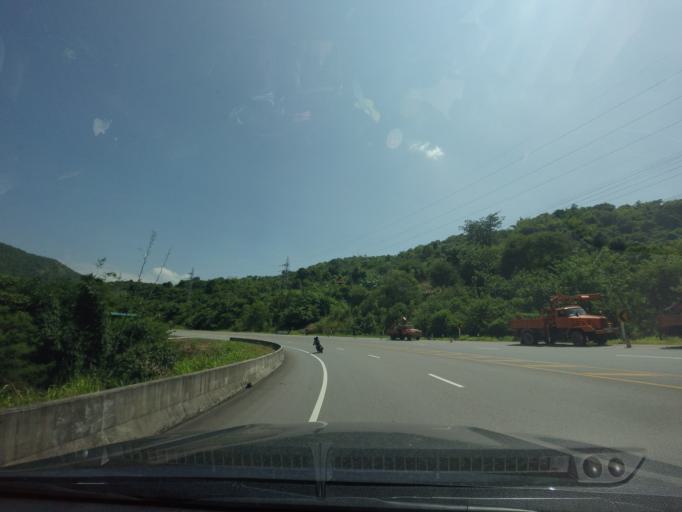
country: TH
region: Phetchabun
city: Lom Sak
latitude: 16.7712
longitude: 101.1269
